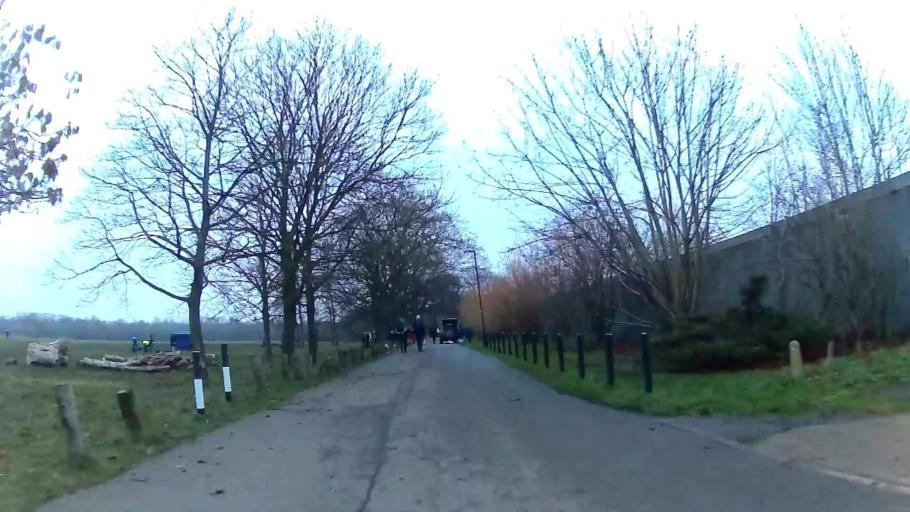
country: GB
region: England
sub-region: Greater London
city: Hammersmith
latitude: 51.5203
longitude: -0.2351
